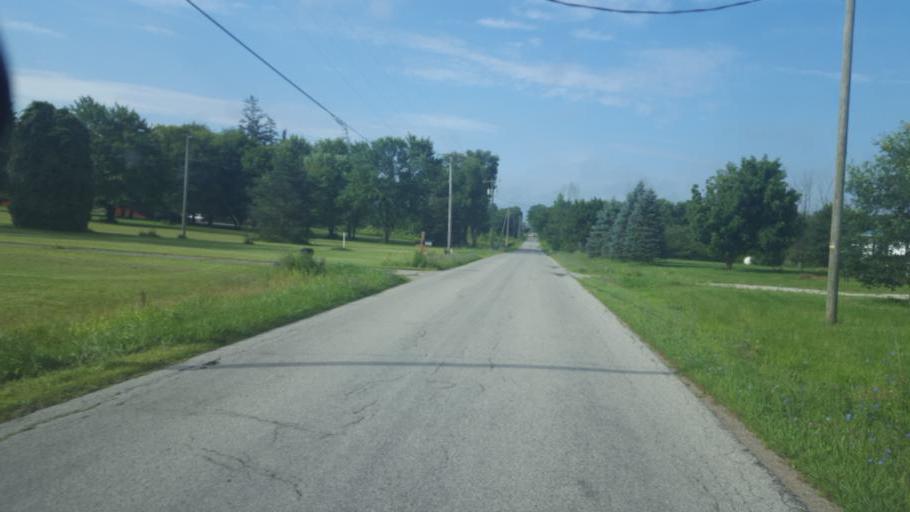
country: US
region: Ohio
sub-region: Morrow County
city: Cardington
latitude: 40.4409
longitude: -82.8481
